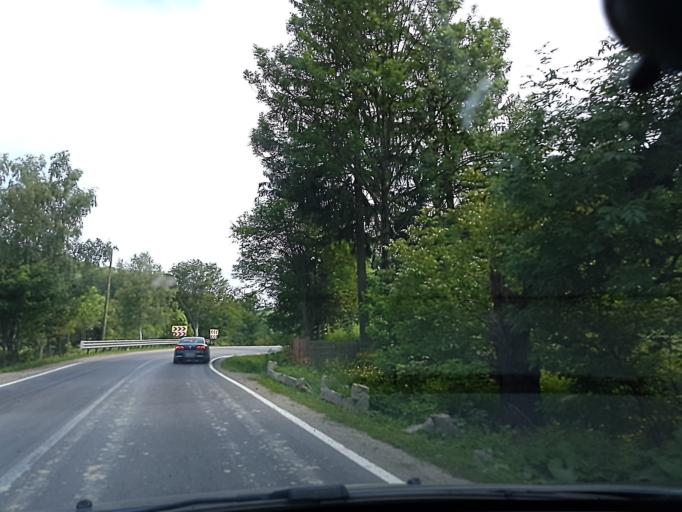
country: RO
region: Prahova
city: Maneciu
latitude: 45.3511
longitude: 25.9478
